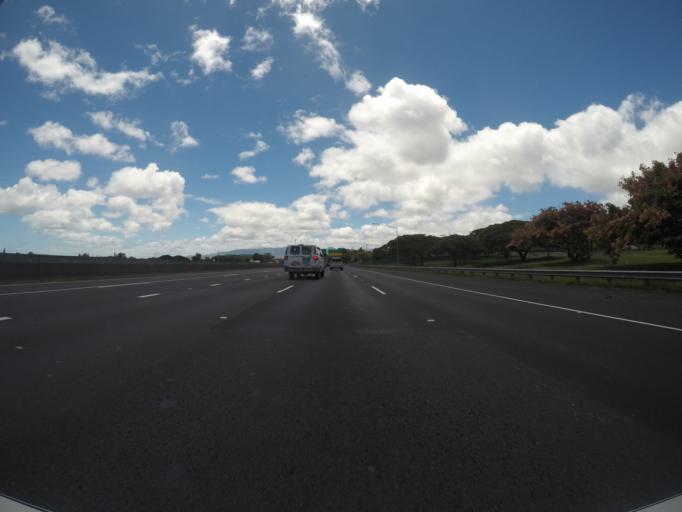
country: US
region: Hawaii
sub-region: Honolulu County
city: Halawa Heights
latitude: 21.3714
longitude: -157.9166
